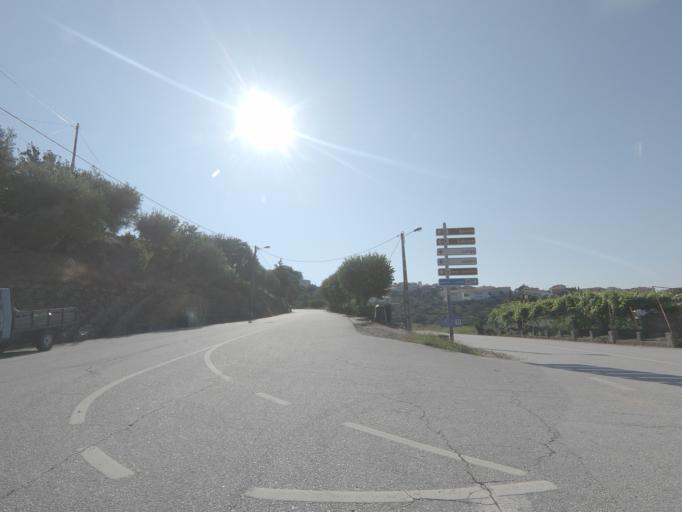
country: PT
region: Viseu
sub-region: Tabuaco
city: Tabuaco
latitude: 41.1157
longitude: -7.5598
